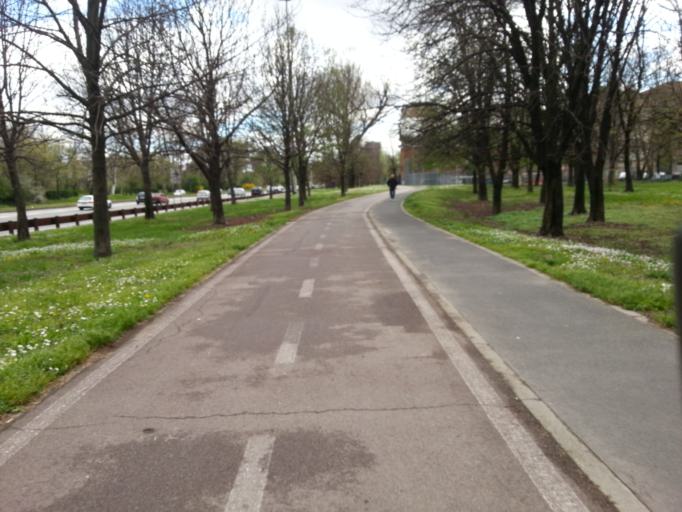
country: IT
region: Lombardy
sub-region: Citta metropolitana di Milano
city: Bresso
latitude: 45.5138
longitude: 9.1789
